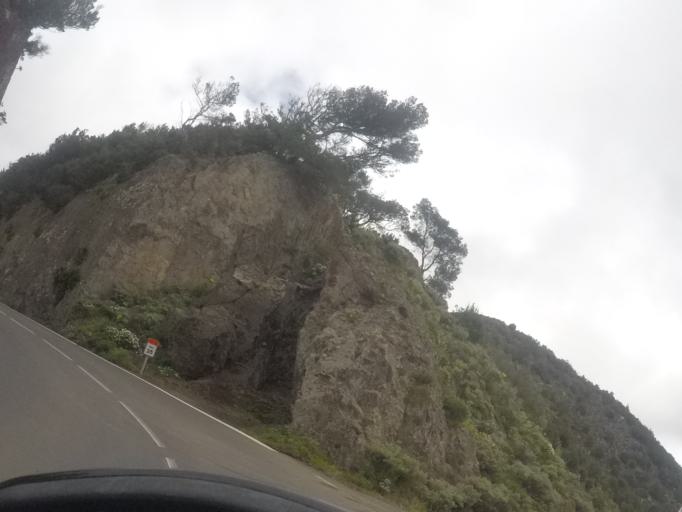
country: ES
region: Canary Islands
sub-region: Provincia de Santa Cruz de Tenerife
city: Tegueste
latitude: 28.5240
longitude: -16.2878
